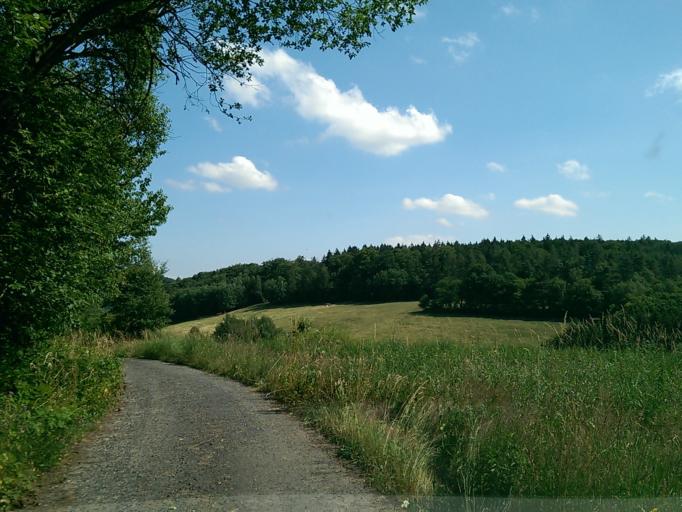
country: CZ
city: Duba
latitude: 50.5024
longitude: 14.5059
